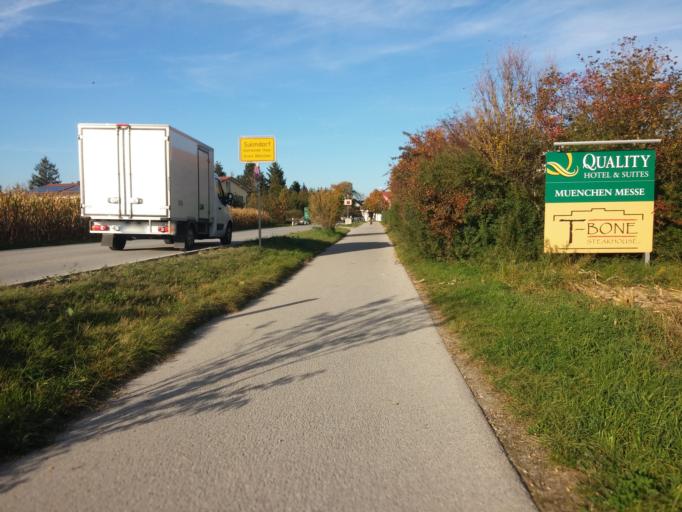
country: DE
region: Bavaria
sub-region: Upper Bavaria
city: Haar
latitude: 48.1275
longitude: 11.7160
